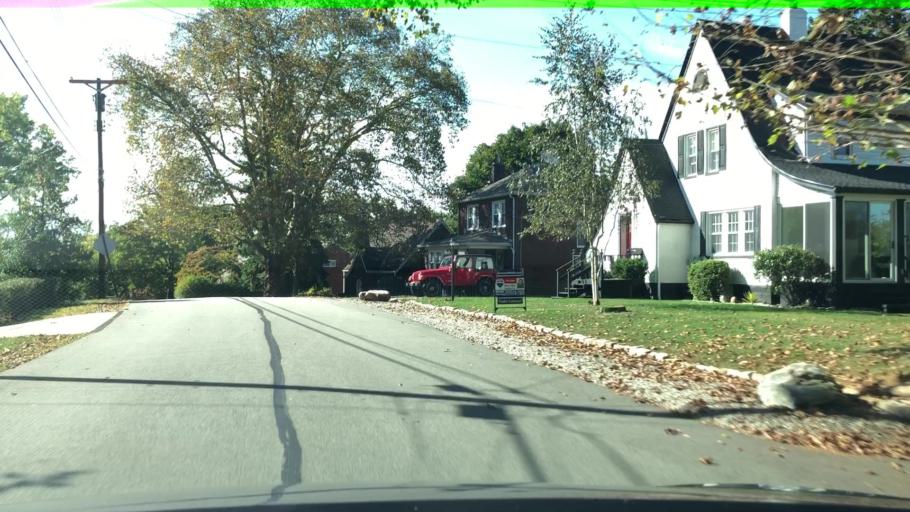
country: US
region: Pennsylvania
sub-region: Allegheny County
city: Penn Hills
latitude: 40.4733
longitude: -79.8220
